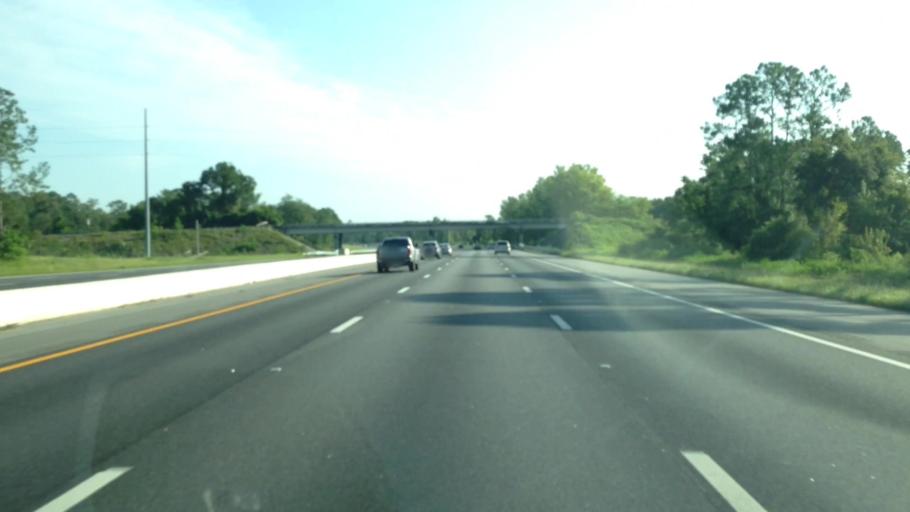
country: US
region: Florida
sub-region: Pasco County
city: Wesley Chapel
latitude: 28.2717
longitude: -82.3277
